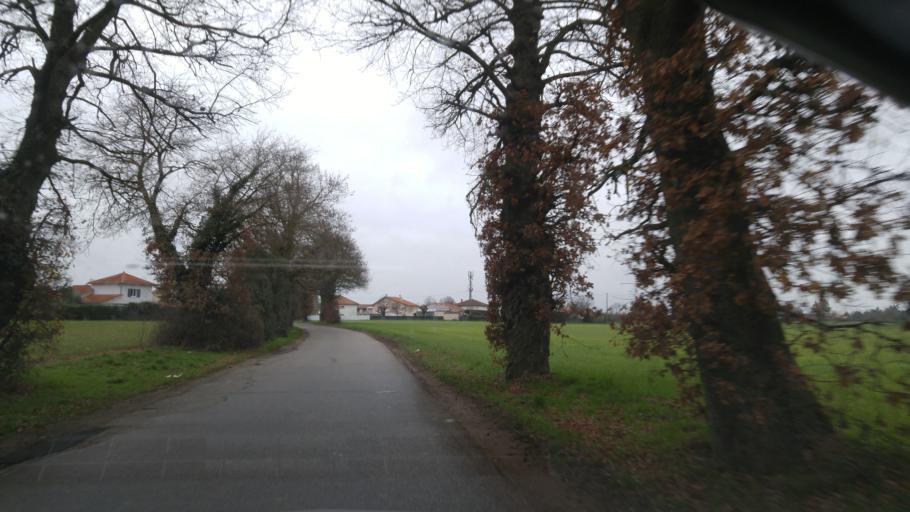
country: FR
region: Rhone-Alpes
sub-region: Departement du Rhone
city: Saint-Laurent-de-Mure
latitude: 45.6995
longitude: 5.0393
